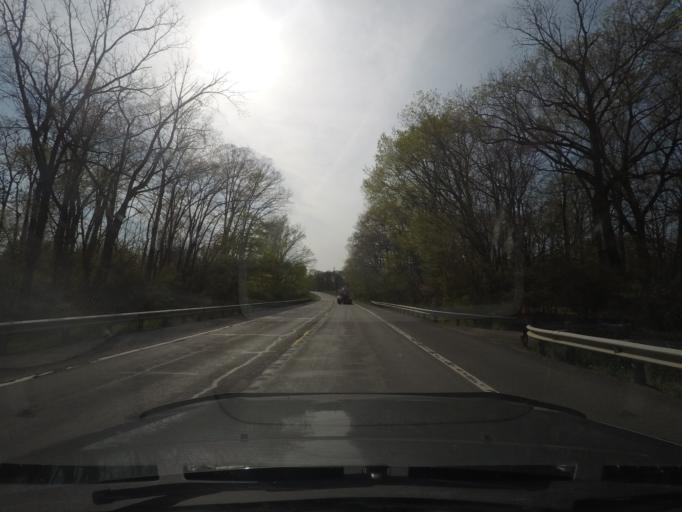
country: US
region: Michigan
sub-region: Berrien County
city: Buchanan
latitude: 41.7976
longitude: -86.4600
